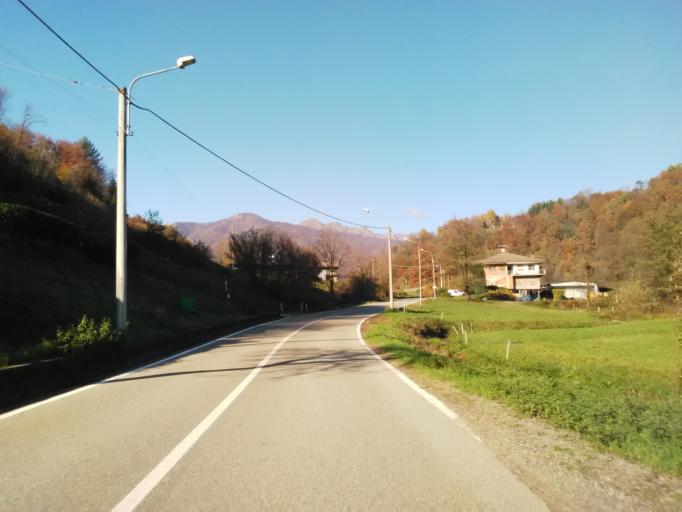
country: IT
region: Piedmont
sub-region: Provincia di Vercelli
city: Borgosesia
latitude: 45.7319
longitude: 8.2822
